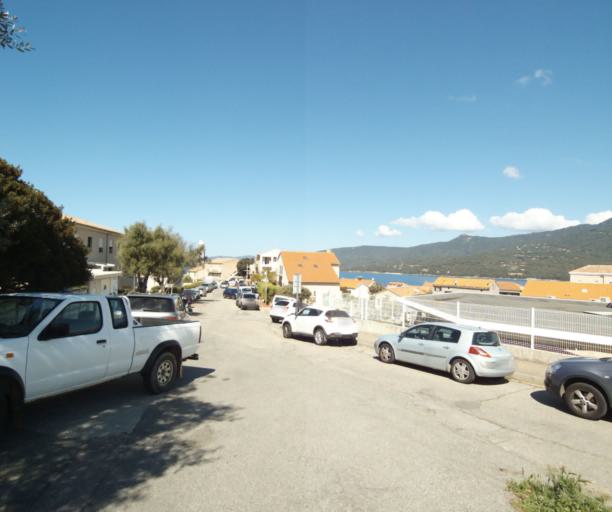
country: FR
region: Corsica
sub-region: Departement de la Corse-du-Sud
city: Propriano
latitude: 41.6745
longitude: 8.9077
